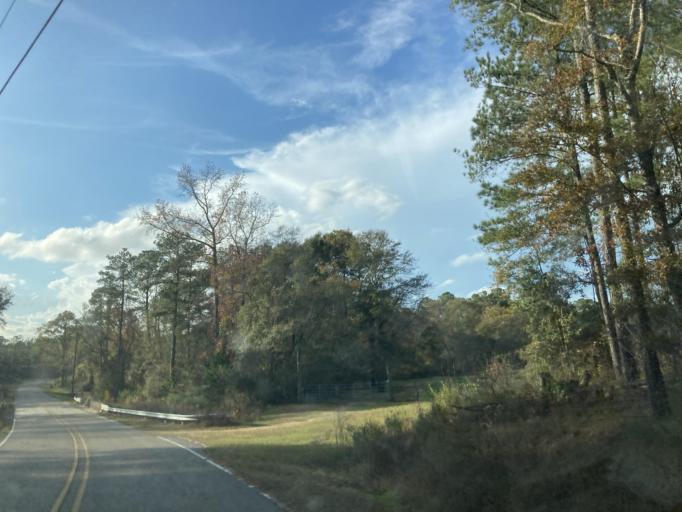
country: US
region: Mississippi
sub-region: Lamar County
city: Purvis
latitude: 31.1421
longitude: -89.6374
